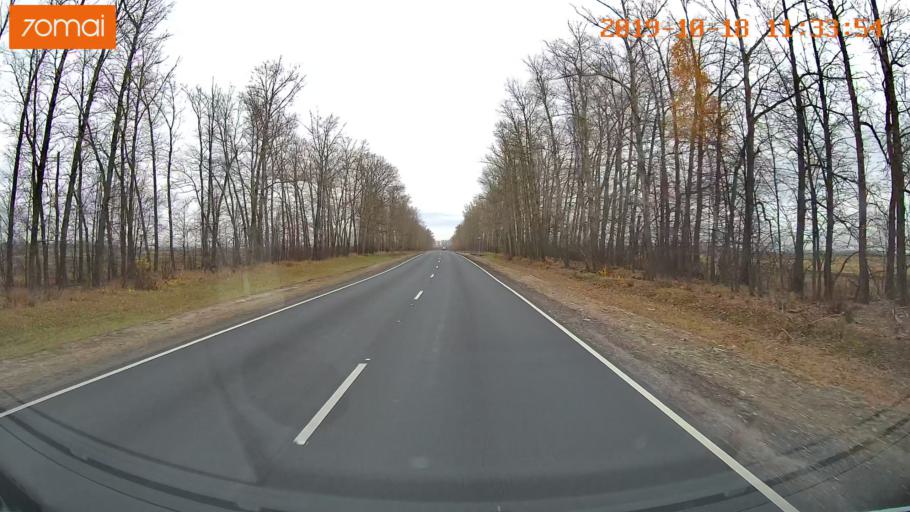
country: RU
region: Rjazan
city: Oktyabr'skiy
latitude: 54.1377
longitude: 38.7517
